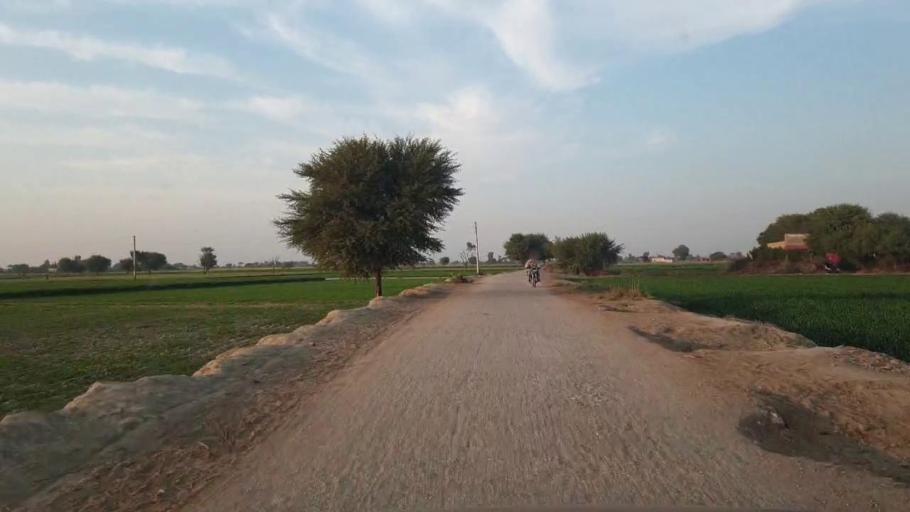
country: PK
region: Sindh
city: Shahpur Chakar
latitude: 26.1853
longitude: 68.6171
